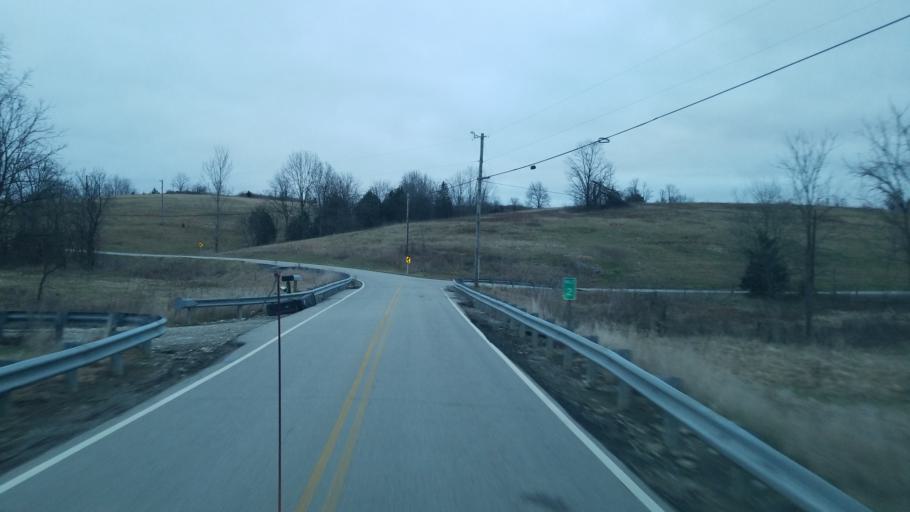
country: US
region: Kentucky
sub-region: Mason County
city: Maysville
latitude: 38.5352
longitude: -83.6954
